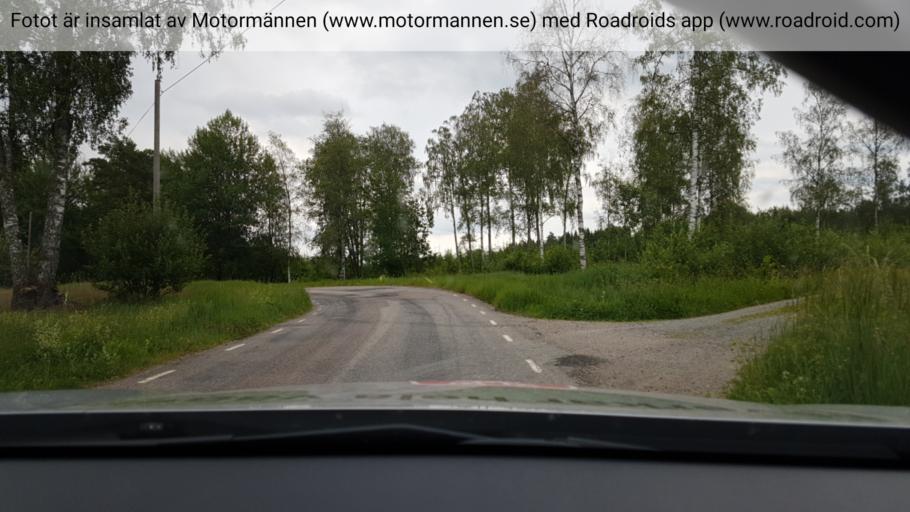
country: SE
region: Joenkoeping
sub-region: Mullsjo Kommun
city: Mullsjoe
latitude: 57.9444
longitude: 13.6658
